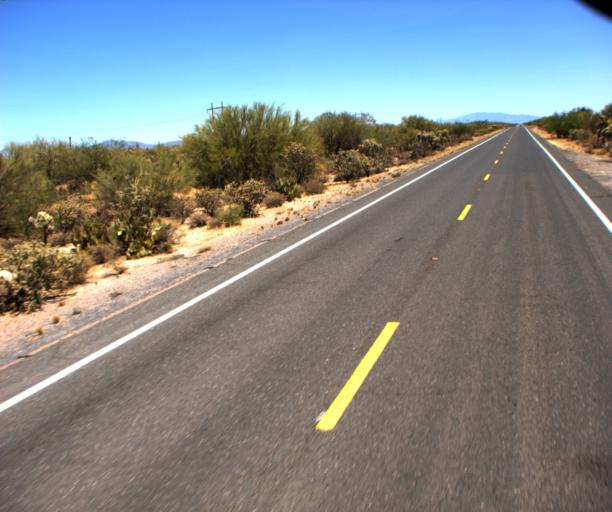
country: US
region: Arizona
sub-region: Pinal County
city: Florence
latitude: 32.8300
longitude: -111.2111
